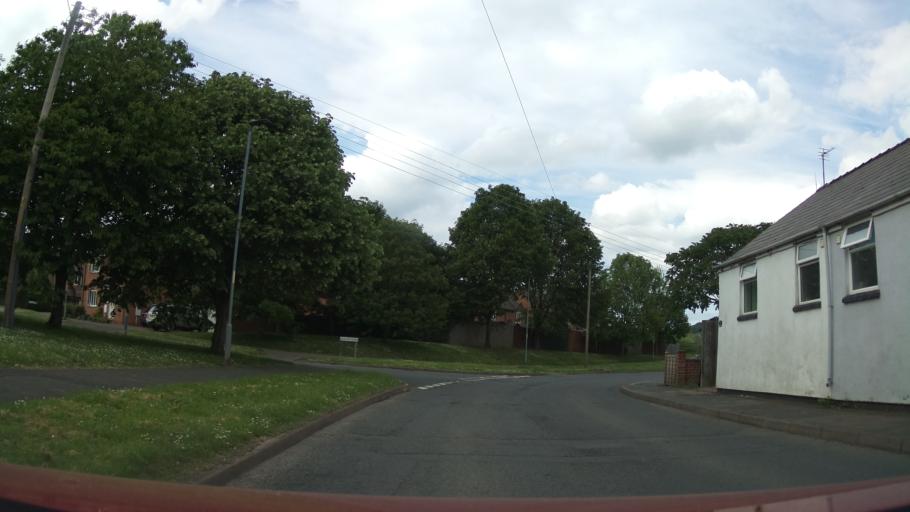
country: GB
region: England
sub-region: Herefordshire
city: Ledbury
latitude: 52.0335
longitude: -2.4385
